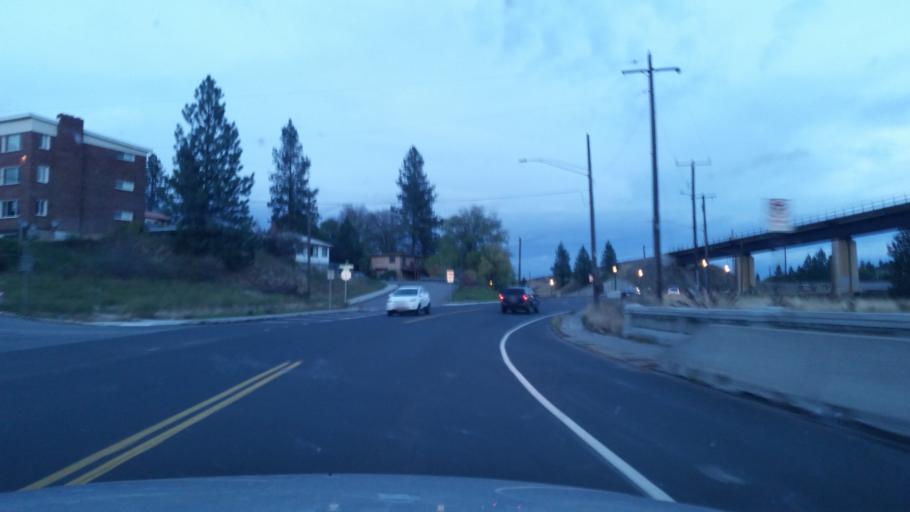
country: US
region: Washington
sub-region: Spokane County
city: Spokane
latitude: 47.6504
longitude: -117.4463
